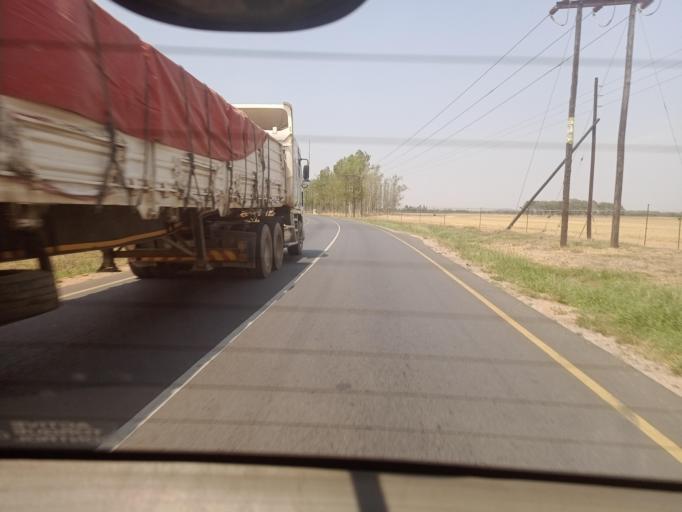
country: ZM
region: Lusaka
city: Lusaka
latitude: -15.2890
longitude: 28.3753
